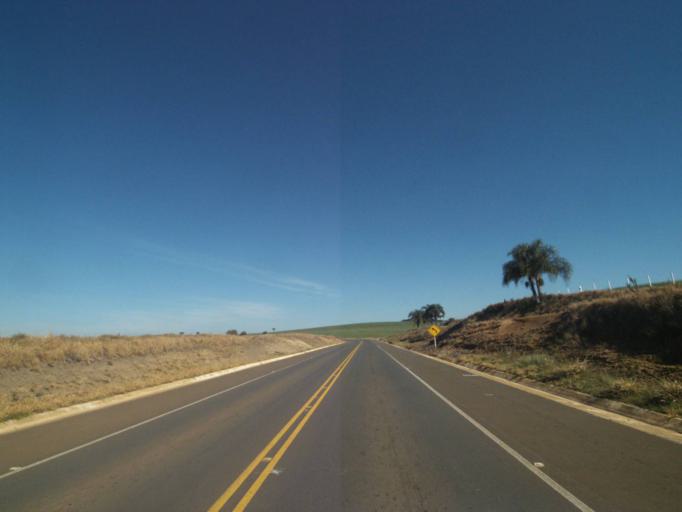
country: BR
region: Parana
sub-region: Tibagi
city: Tibagi
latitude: -24.6319
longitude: -50.4577
